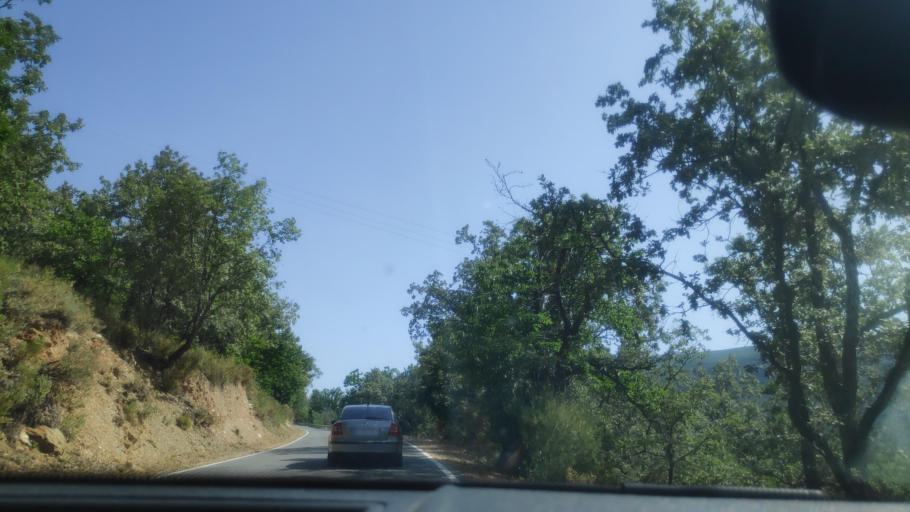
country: ES
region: Andalusia
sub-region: Provincia de Granada
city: Busquistar
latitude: 36.9540
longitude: -3.2788
